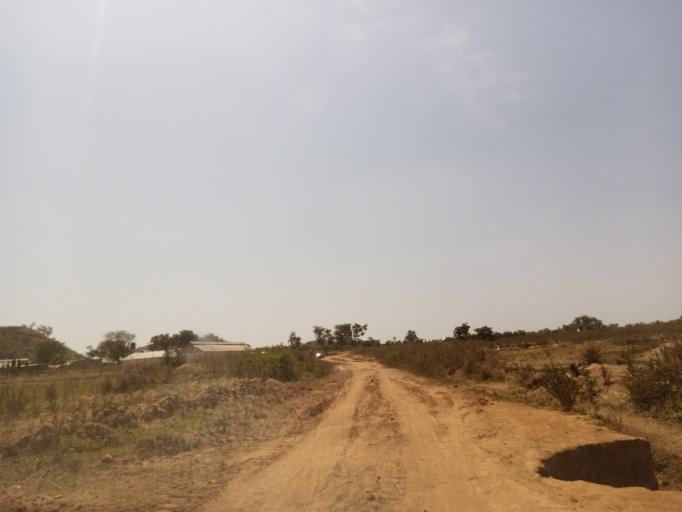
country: NG
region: Abuja Federal Capital Territory
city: Kuje
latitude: 8.9075
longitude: 7.3367
